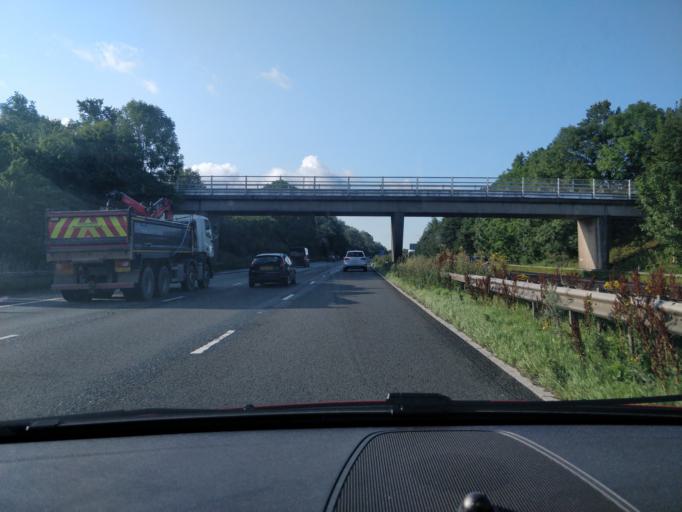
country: GB
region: England
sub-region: Knowsley
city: Knowsley
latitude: 53.4462
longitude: -2.8603
